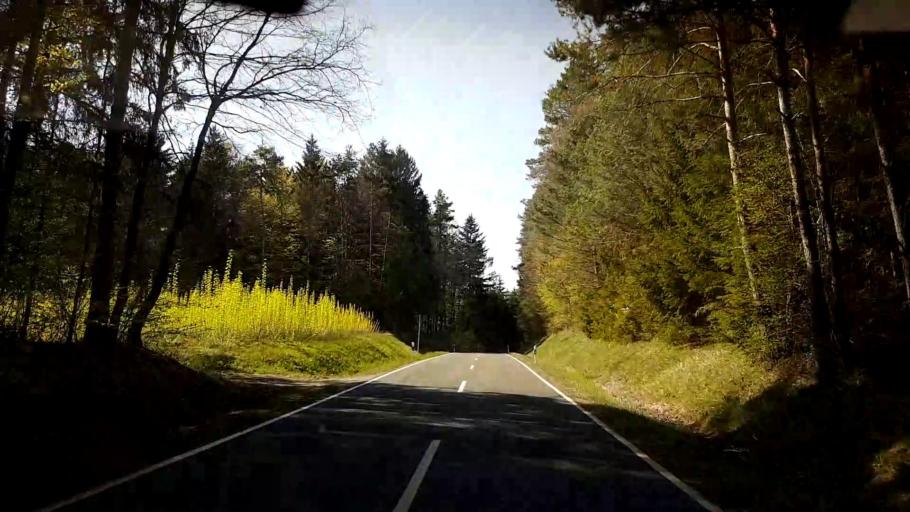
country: DE
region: Bavaria
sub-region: Upper Franconia
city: Pottenstein
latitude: 49.7929
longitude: 11.4114
